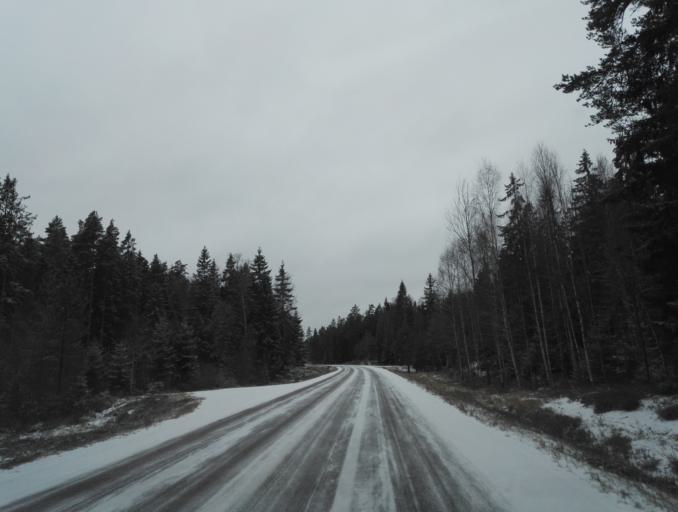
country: SE
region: Kronoberg
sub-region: Lessebo Kommun
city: Lessebo
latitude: 56.7330
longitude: 15.2333
